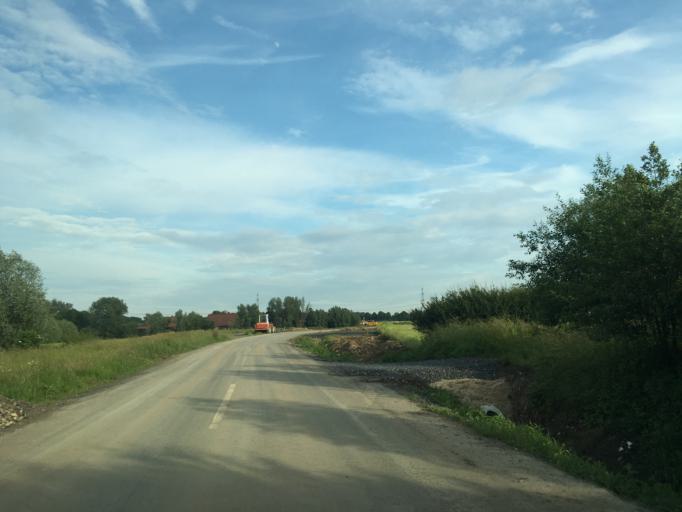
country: DE
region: North Rhine-Westphalia
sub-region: Regierungsbezirk Munster
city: Altenberge
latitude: 51.9723
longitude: 7.5253
